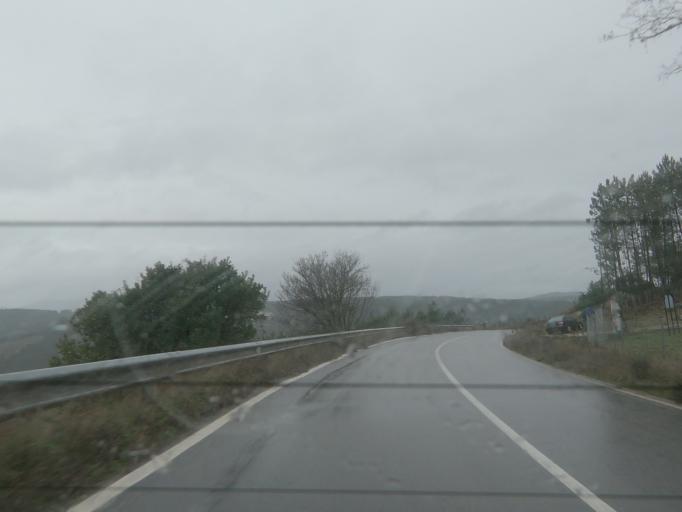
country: PT
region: Vila Real
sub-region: Vila Real
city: Vila Real
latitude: 41.2406
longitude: -7.6889
